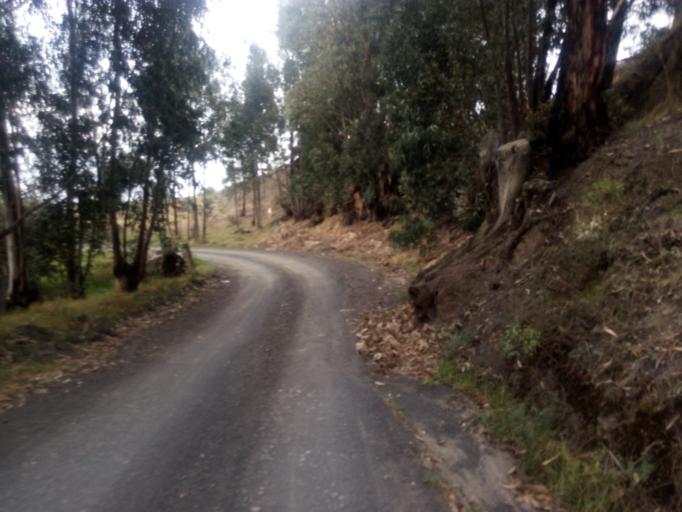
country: CO
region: Boyaca
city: Chita
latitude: 6.1924
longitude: -72.4900
